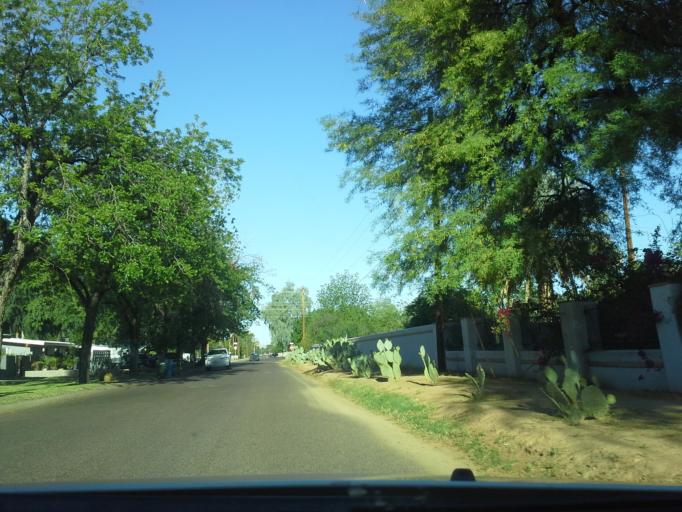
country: US
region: Arizona
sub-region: Maricopa County
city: Phoenix
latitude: 33.5422
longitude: -112.0897
